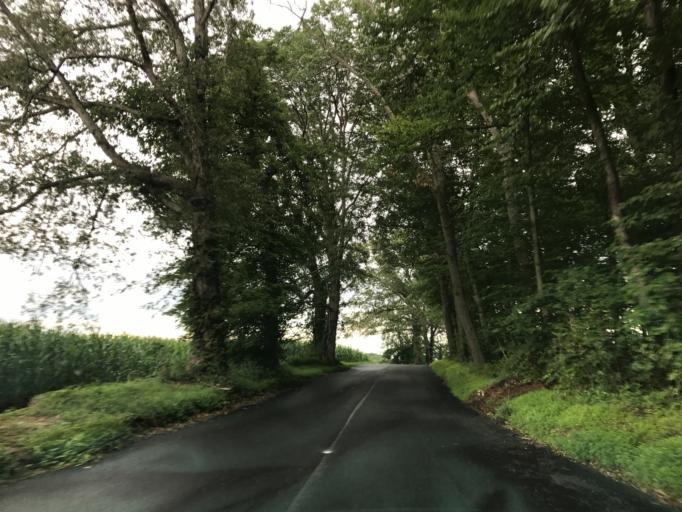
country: US
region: Pennsylvania
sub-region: York County
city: New Freedom
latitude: 39.6770
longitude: -76.7458
